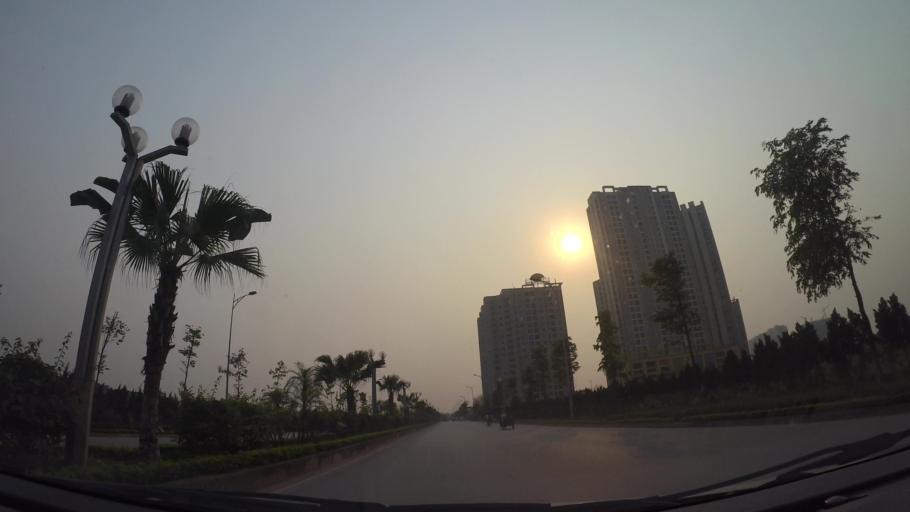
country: VN
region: Ha Noi
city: Cau Dien
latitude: 21.0051
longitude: 105.7301
